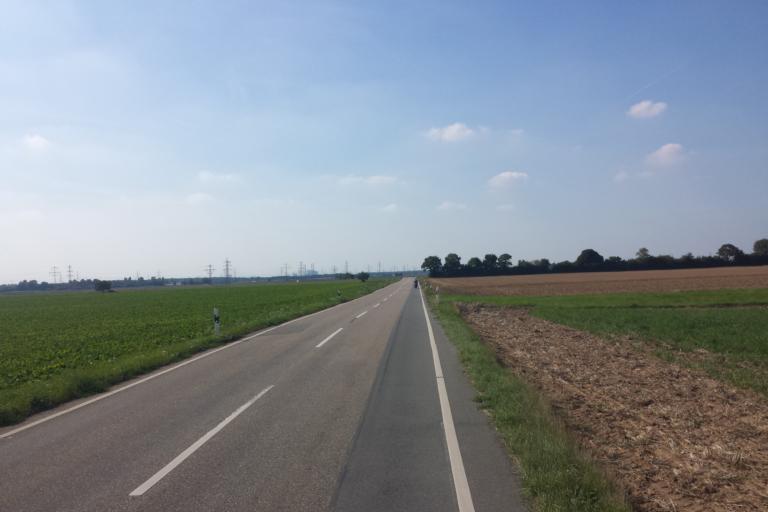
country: DE
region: Baden-Wuerttemberg
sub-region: Karlsruhe Region
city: Eppelheim
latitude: 49.4174
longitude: 8.6174
